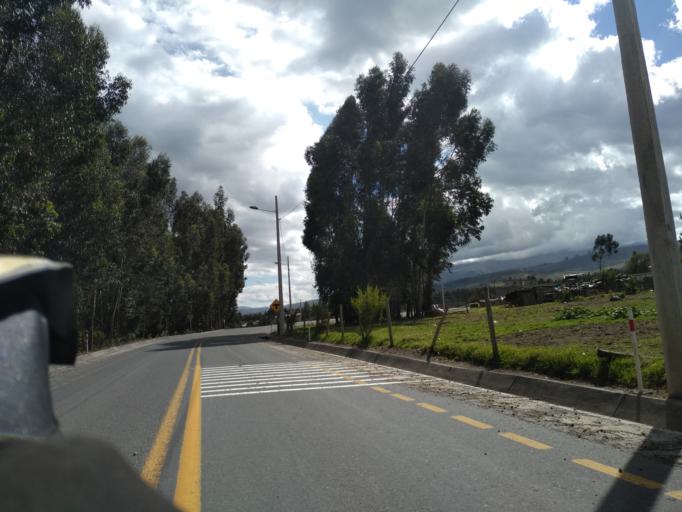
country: EC
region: Cotopaxi
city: Saquisili
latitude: -0.7030
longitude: -78.5829
